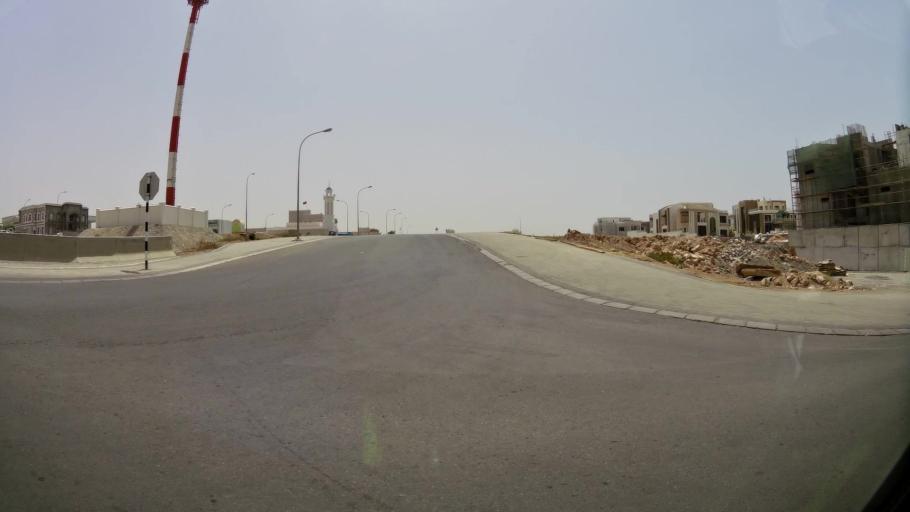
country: OM
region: Muhafazat Masqat
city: Bawshar
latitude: 23.5618
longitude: 58.3977
